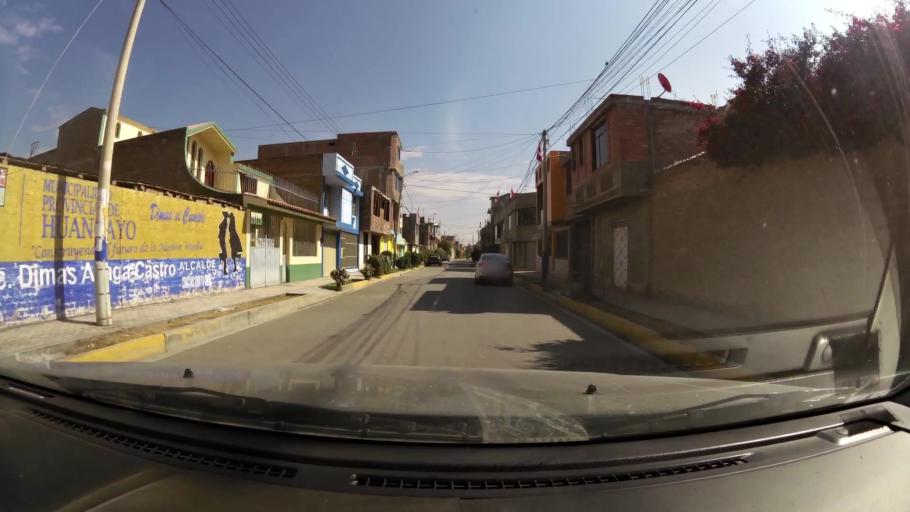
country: PE
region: Junin
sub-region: Provincia de Huancayo
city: El Tambo
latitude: -12.0745
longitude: -75.2254
